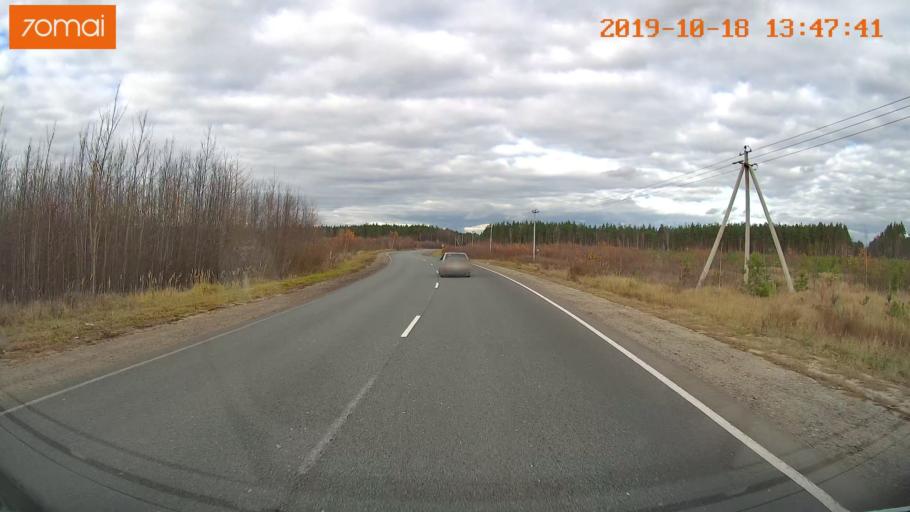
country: RU
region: Moskovskaya
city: Radovitskiy
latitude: 54.9785
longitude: 39.9513
